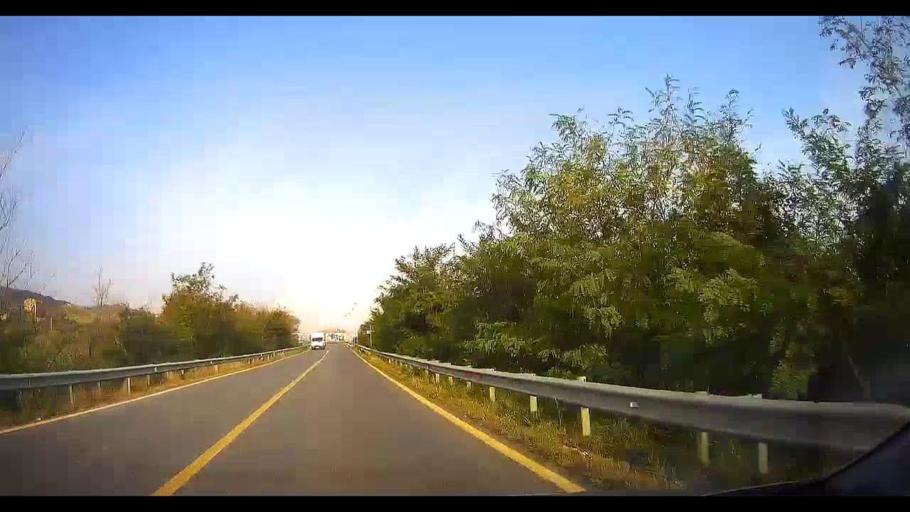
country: IT
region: Calabria
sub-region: Provincia di Cosenza
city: Cariati
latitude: 39.5224
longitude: 16.8990
